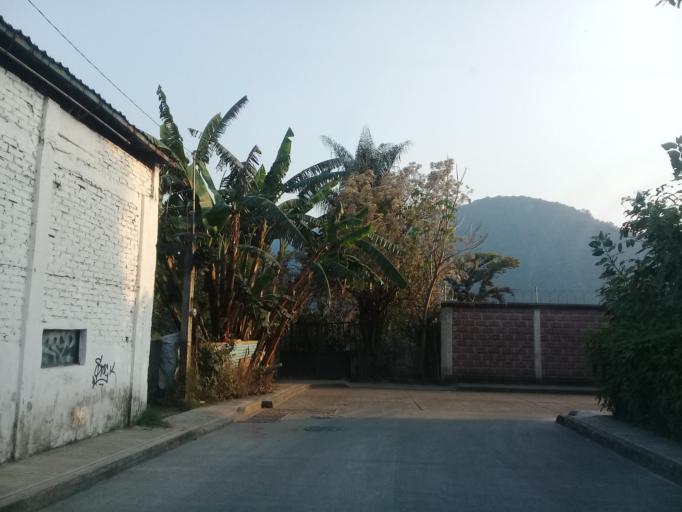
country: MX
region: Veracruz
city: Ixtac Zoquitlan
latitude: 18.8500
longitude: -97.0572
